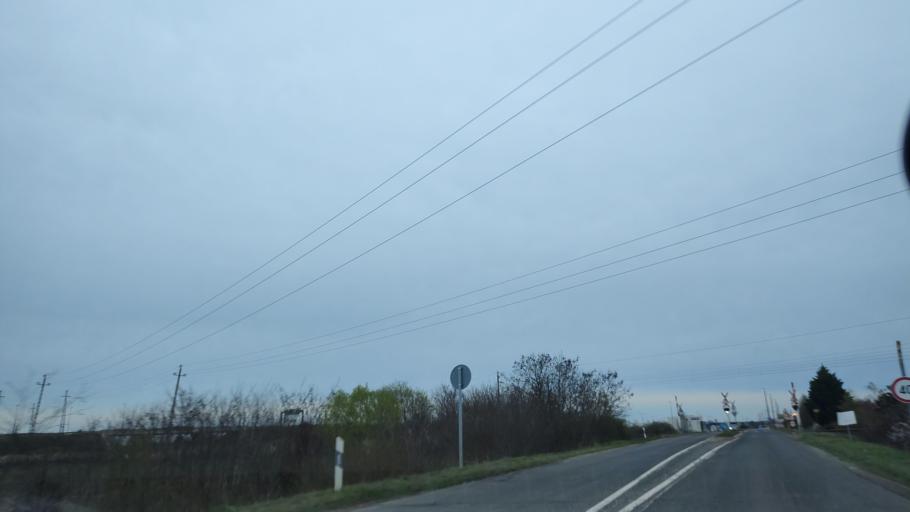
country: HU
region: Vas
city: Szombathely
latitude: 47.2476
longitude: 16.6505
